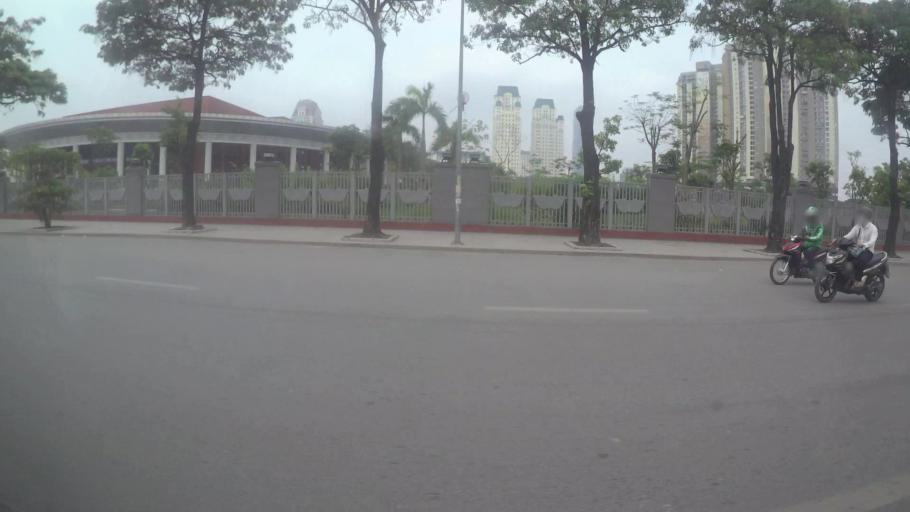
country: VN
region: Ha Noi
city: Cau Dien
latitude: 21.0118
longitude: 105.7716
